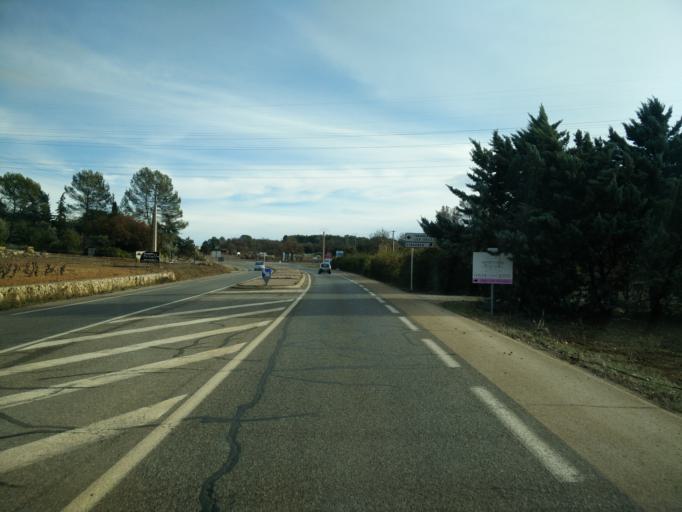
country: FR
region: Provence-Alpes-Cote d'Azur
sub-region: Departement du Var
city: Lorgues
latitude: 43.4675
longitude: 6.3863
